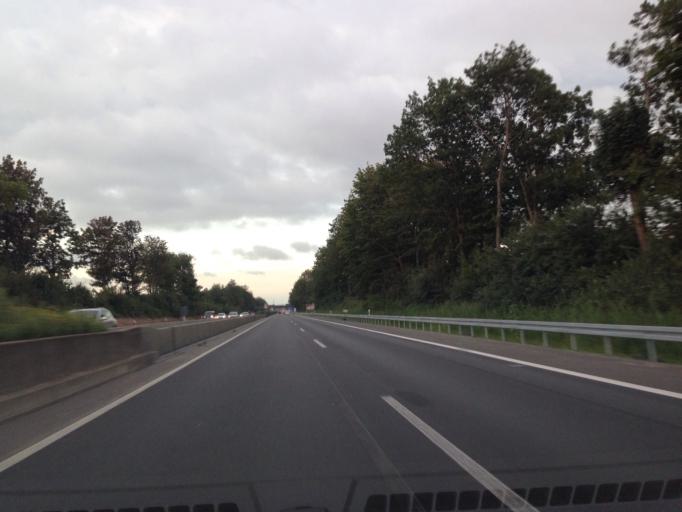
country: DE
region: North Rhine-Westphalia
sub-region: Regierungsbezirk Dusseldorf
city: Neubrueck
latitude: 51.1497
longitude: 6.6293
